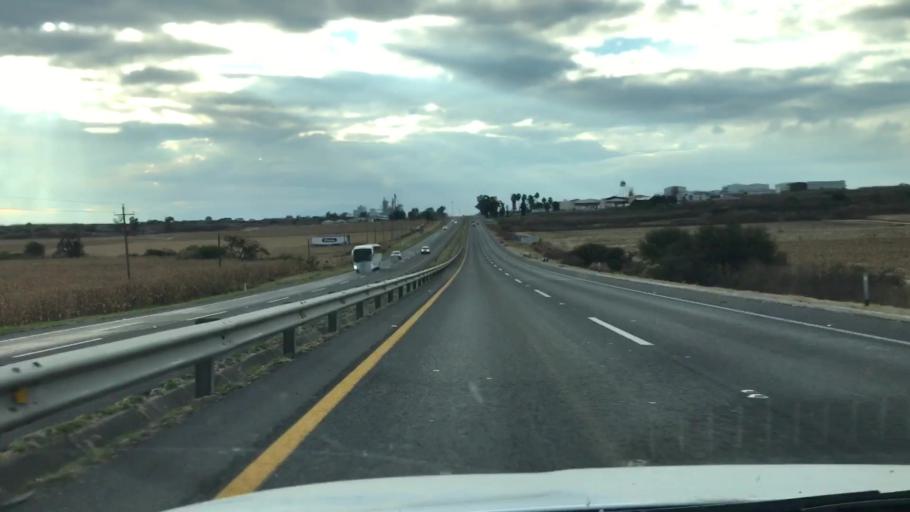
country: MX
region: Guanajuato
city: Penjamo
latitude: 20.3819
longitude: -101.8131
